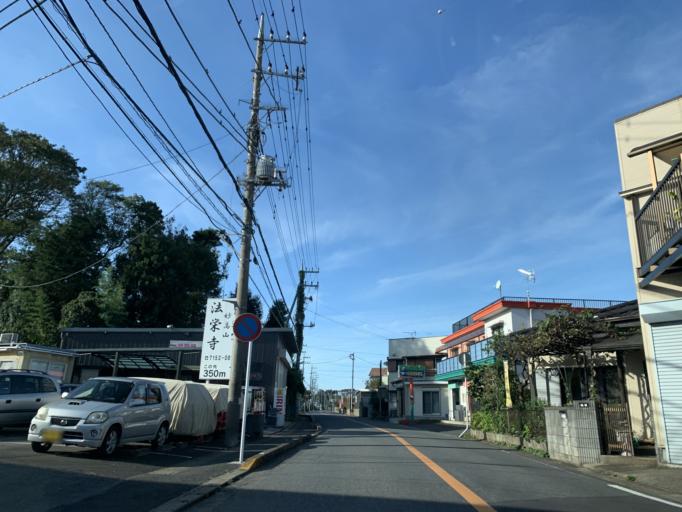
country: JP
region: Chiba
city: Nagareyama
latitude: 35.8884
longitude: 139.9335
